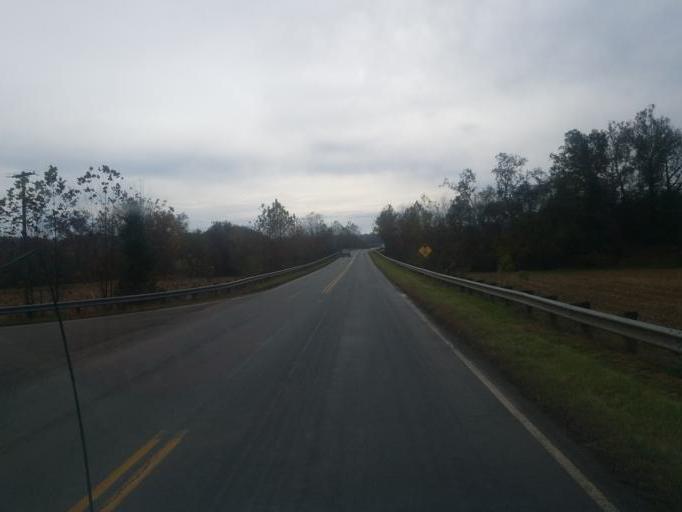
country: US
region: Ohio
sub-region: Washington County
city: Beverly
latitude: 39.5465
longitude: -81.6456
